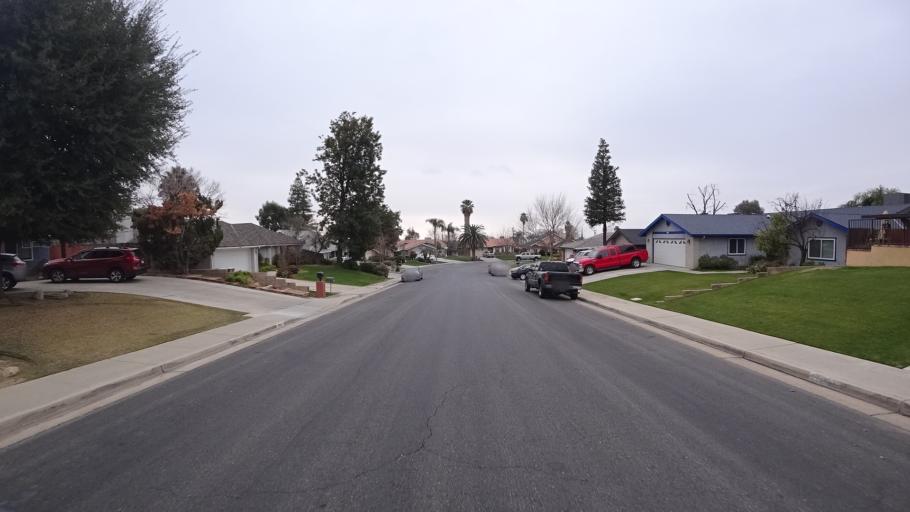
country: US
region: California
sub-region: Kern County
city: Bakersfield
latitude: 35.3808
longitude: -118.9334
